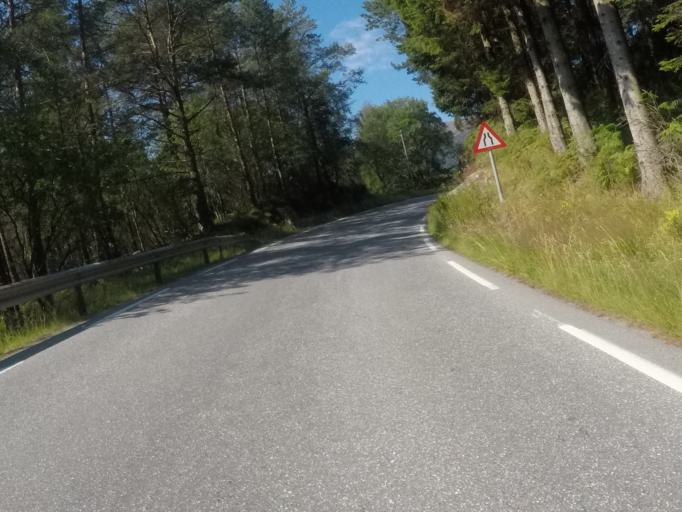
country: NO
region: Sogn og Fjordane
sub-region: Bremanger
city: Svelgen
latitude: 61.7380
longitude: 5.1807
